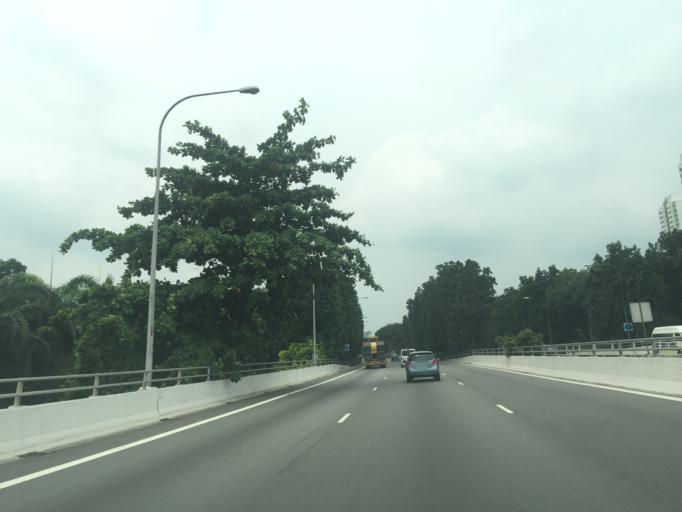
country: MY
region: Johor
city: Johor Bahru
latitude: 1.3888
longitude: 103.7557
